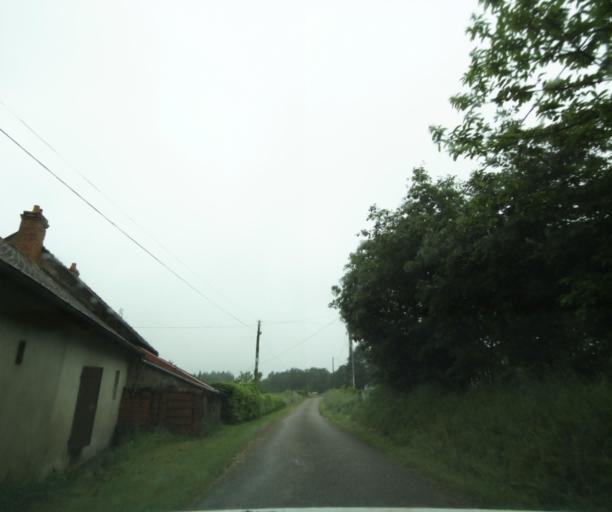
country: FR
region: Bourgogne
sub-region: Departement de Saone-et-Loire
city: Charolles
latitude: 46.4220
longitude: 4.3725
